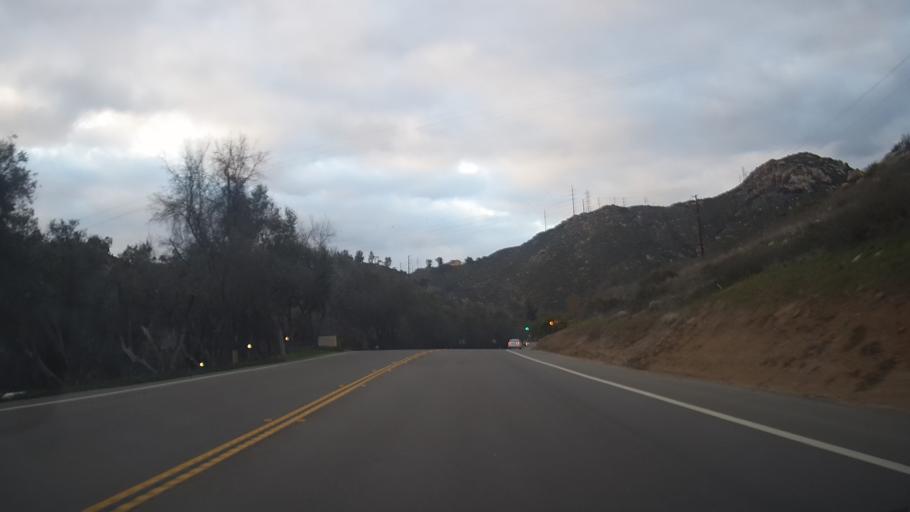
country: US
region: California
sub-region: San Diego County
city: Granite Hills
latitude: 32.7867
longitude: -116.8850
